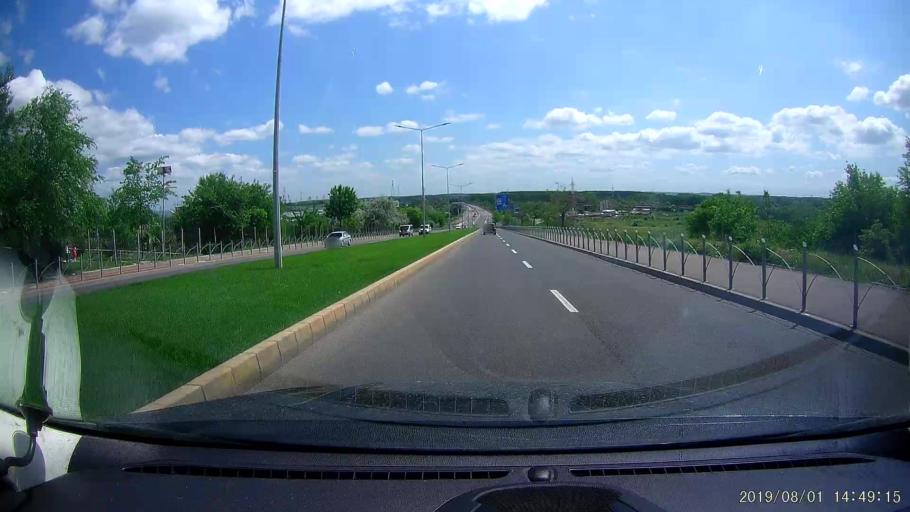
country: RO
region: Galati
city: Galati
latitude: 45.4077
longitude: 28.0151
